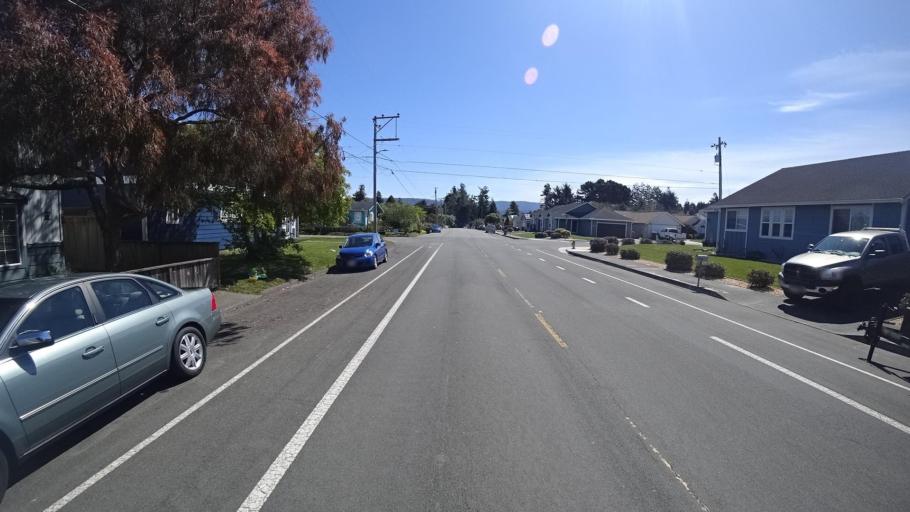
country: US
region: California
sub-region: Humboldt County
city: Myrtletown
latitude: 40.7878
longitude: -124.1267
